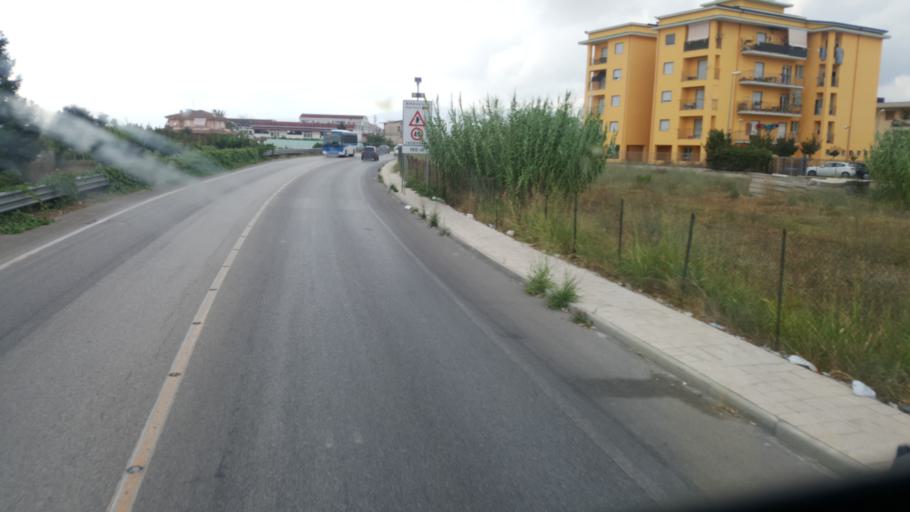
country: IT
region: Campania
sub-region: Provincia di Salerno
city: Battipaglia
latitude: 40.6028
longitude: 14.9743
